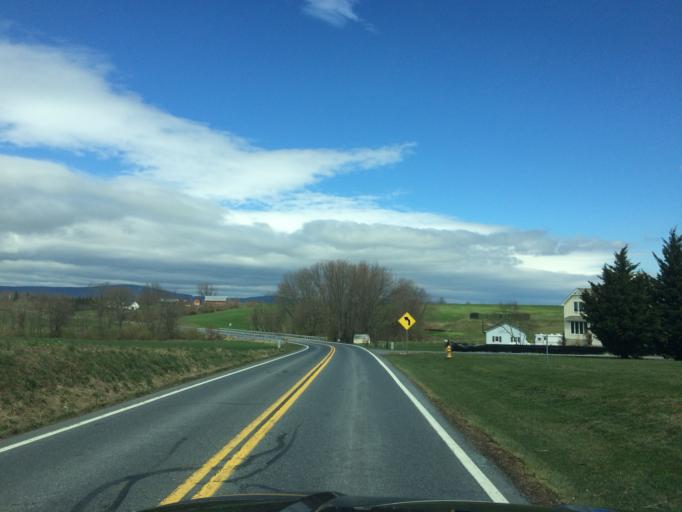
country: US
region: Maryland
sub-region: Frederick County
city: Jefferson
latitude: 39.3623
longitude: -77.5472
